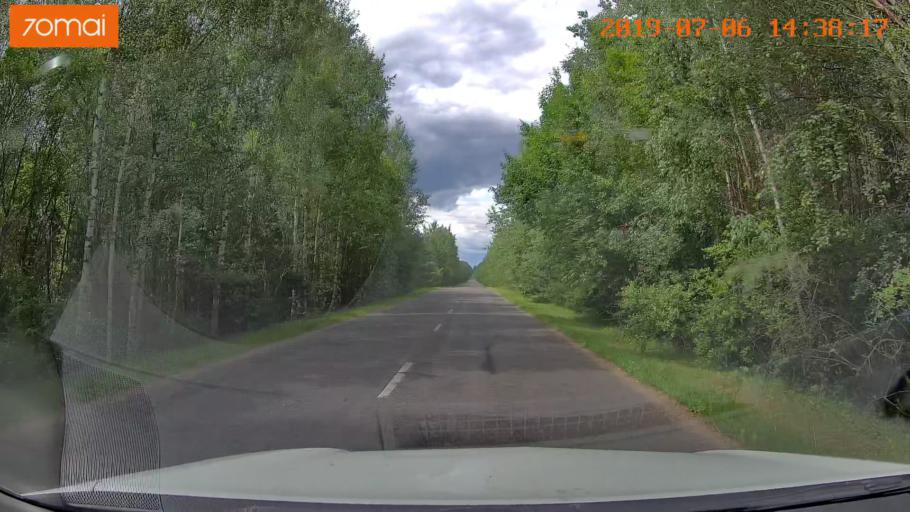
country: BY
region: Minsk
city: Ivyanyets
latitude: 53.9043
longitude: 26.7049
